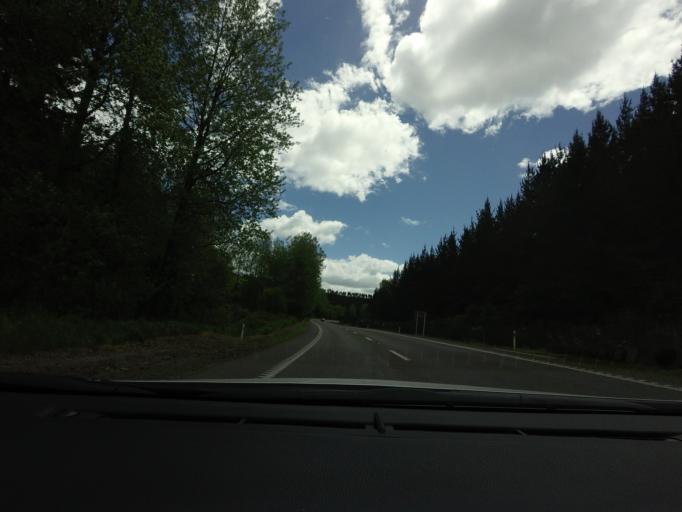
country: NZ
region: Bay of Plenty
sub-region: Rotorua District
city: Rotorua
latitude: -38.2278
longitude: 176.2953
